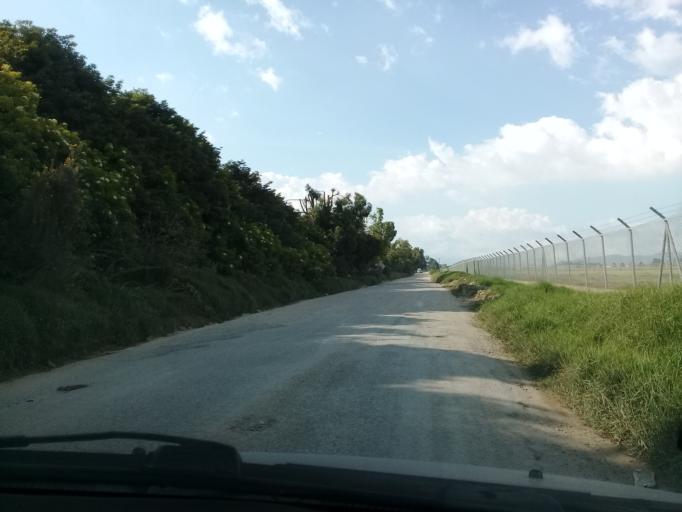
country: CO
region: Cundinamarca
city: Funza
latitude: 4.7136
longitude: -74.1749
